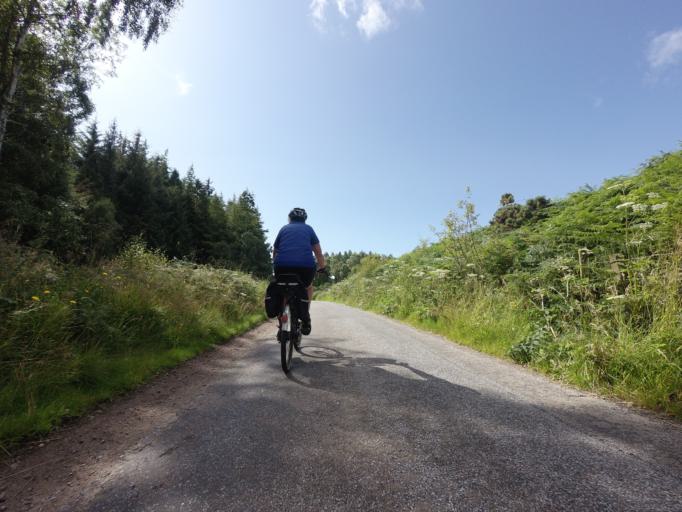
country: GB
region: Scotland
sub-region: Highland
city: Nairn
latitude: 57.5364
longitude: -3.8664
